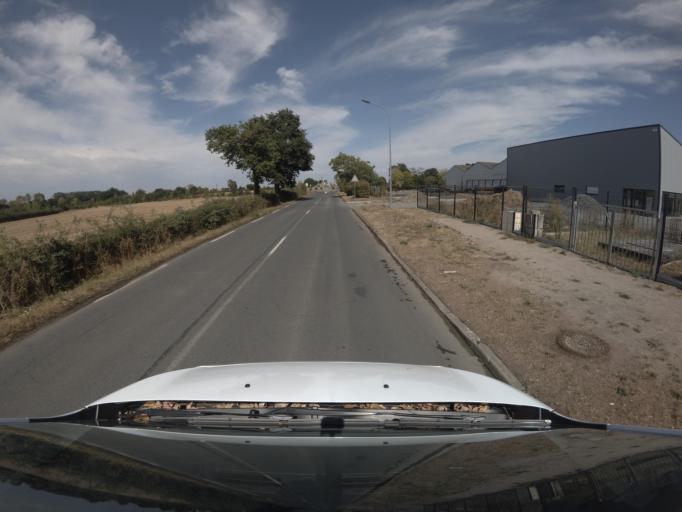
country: FR
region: Poitou-Charentes
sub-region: Departement des Deux-Sevres
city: Nueil-les-Aubiers
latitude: 46.9585
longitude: -0.5837
